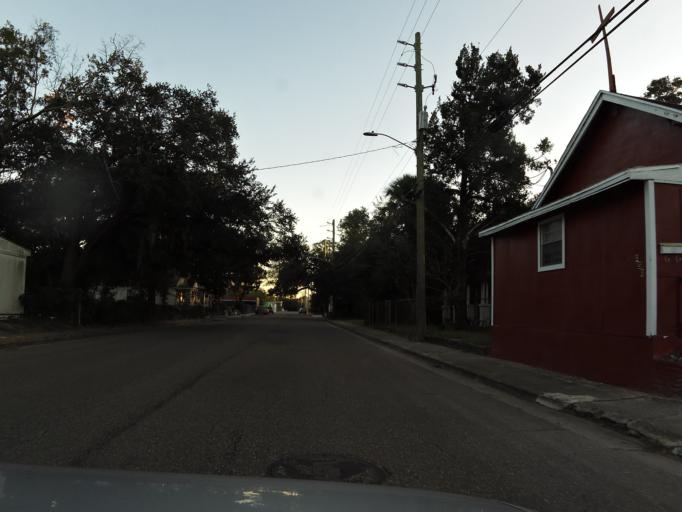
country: US
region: Florida
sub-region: Duval County
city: Jacksonville
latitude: 30.3488
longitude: -81.6411
